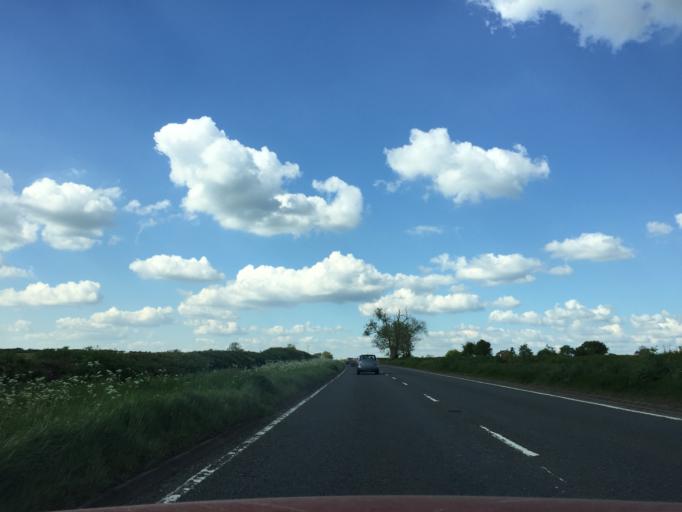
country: GB
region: England
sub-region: Milton Keynes
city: Stony Stratford
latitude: 52.0750
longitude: -0.8618
